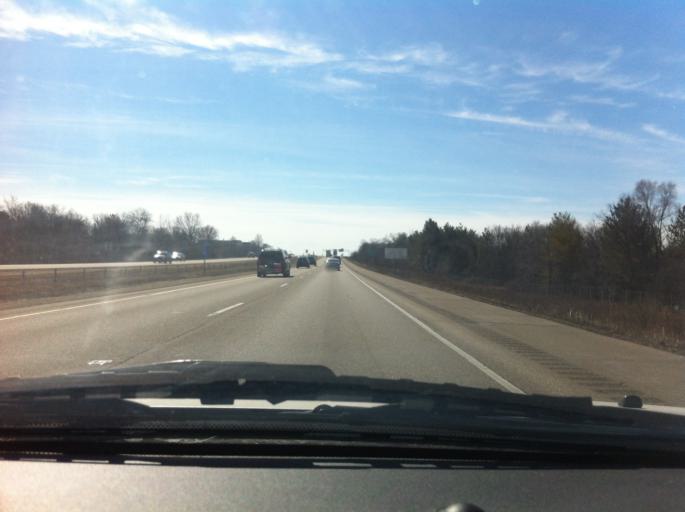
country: US
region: Wisconsin
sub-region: Rock County
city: Janesville
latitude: 42.7303
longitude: -88.9994
